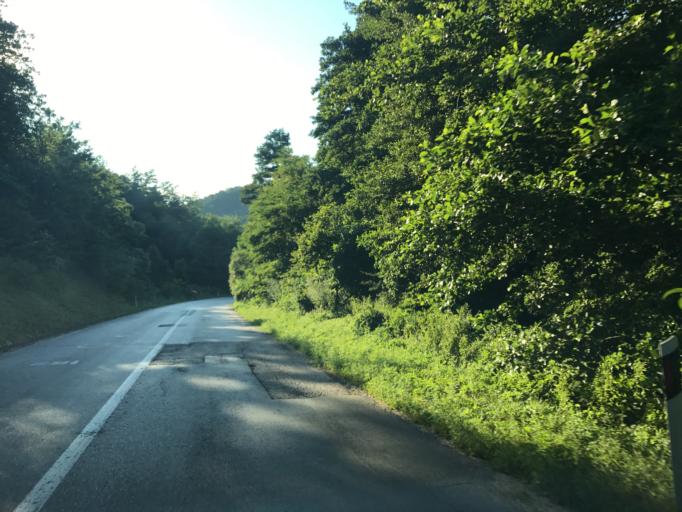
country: RO
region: Mehedinti
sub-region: Comuna Svinita
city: Svinita
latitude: 44.2932
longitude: 22.2620
